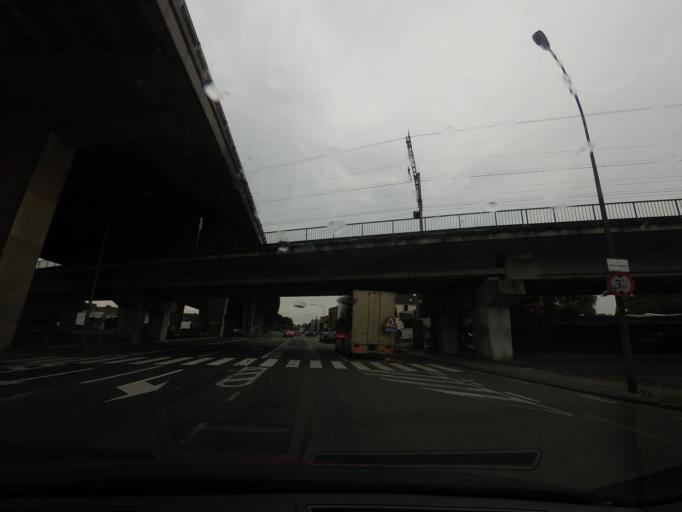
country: BE
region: Flanders
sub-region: Provincie Oost-Vlaanderen
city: Ledeberg
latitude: 51.0362
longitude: 3.7584
